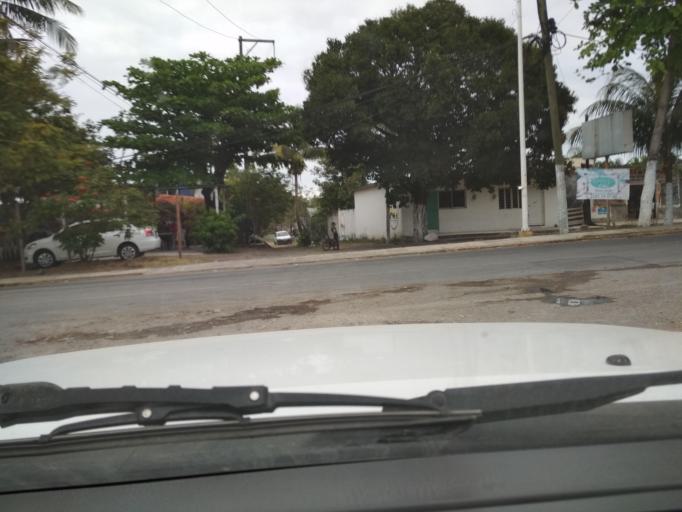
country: MX
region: Veracruz
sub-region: Medellin
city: Fraccionamiento Arboledas San Ramon
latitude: 19.0865
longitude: -96.1536
